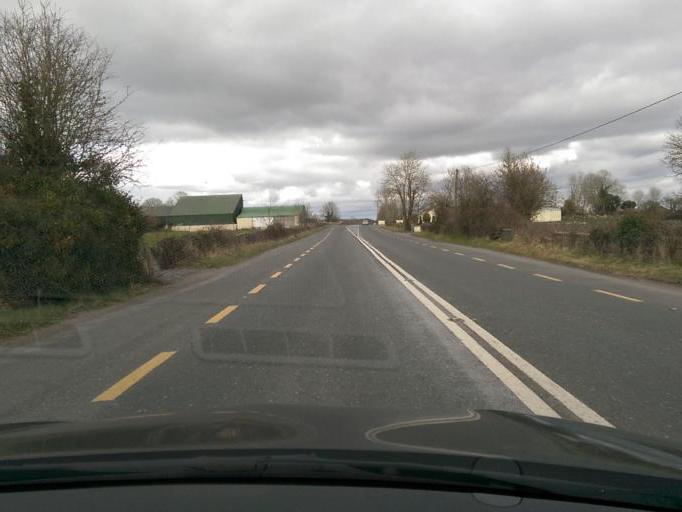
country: IE
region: Connaught
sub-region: County Galway
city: Ballinasloe
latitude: 53.3501
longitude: -8.0850
